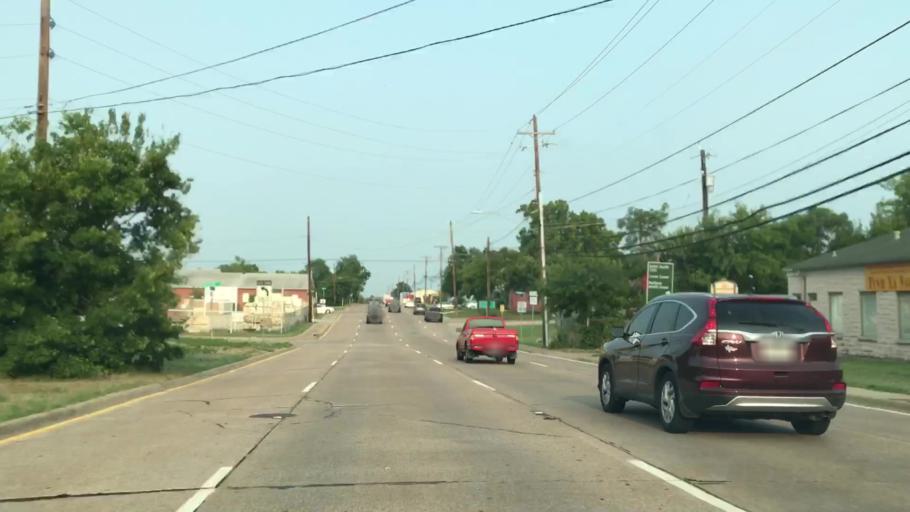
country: US
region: Texas
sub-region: Dallas County
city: Garland
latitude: 32.9089
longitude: -96.6298
